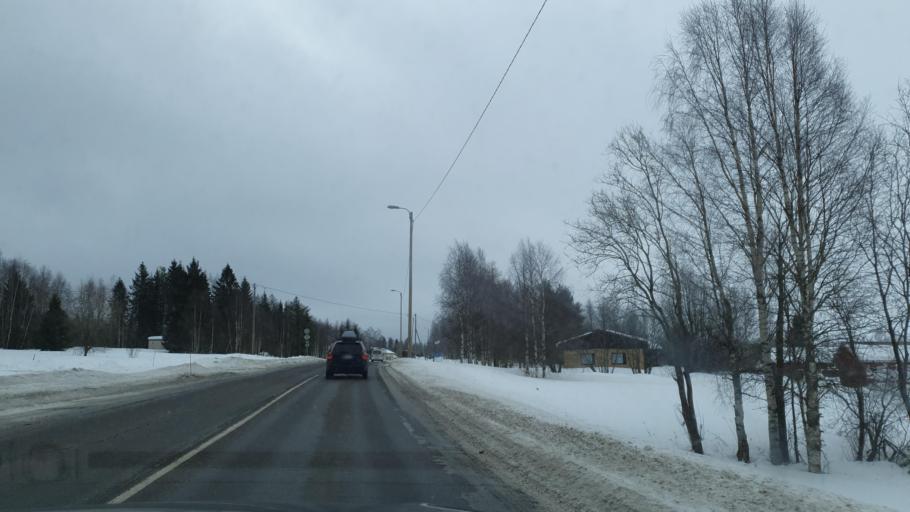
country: FI
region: Lapland
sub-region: Torniolaakso
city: Ylitornio
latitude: 66.2344
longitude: 23.7573
